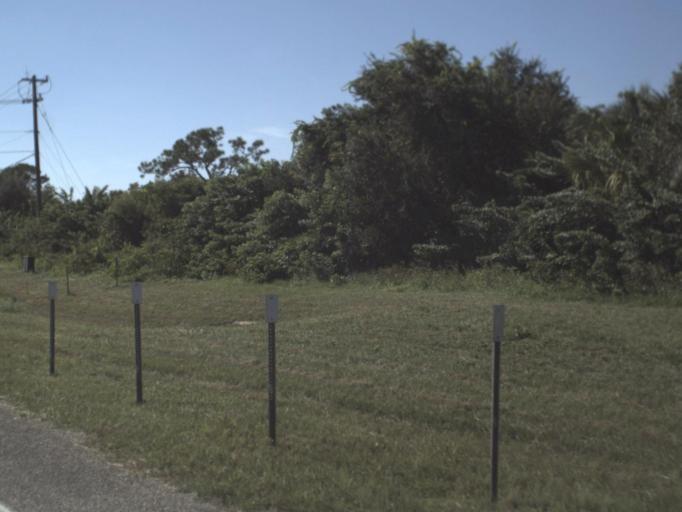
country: US
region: Florida
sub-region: Sarasota County
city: North Port
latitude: 26.9958
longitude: -82.1964
